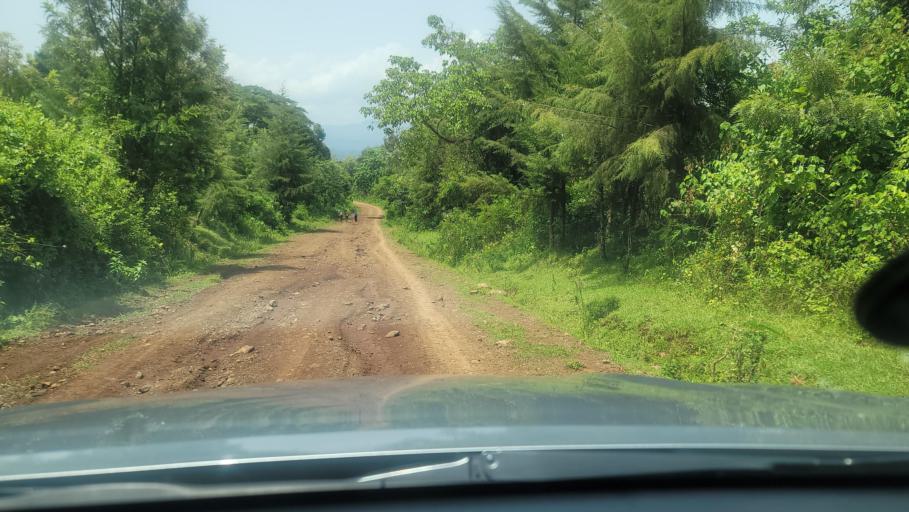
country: ET
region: Oromiya
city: Agaro
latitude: 7.8075
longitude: 36.4132
